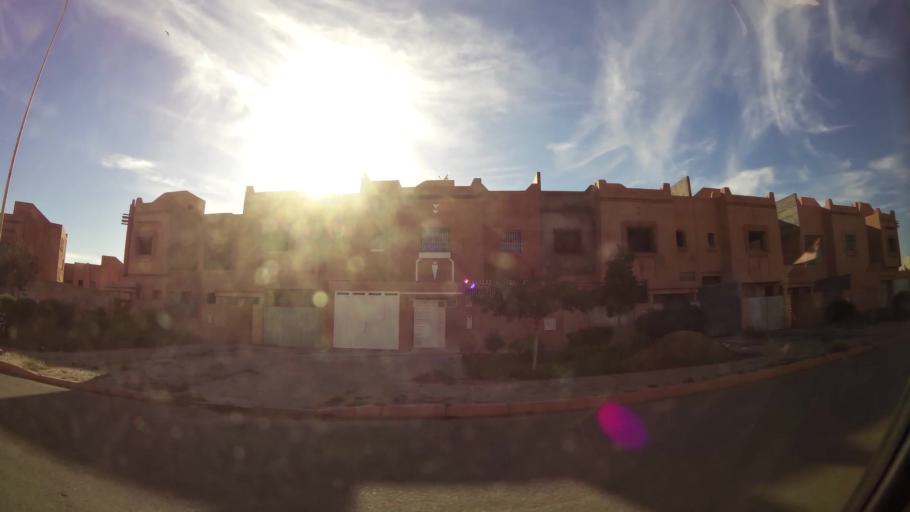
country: MA
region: Marrakech-Tensift-Al Haouz
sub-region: Marrakech
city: Marrakesh
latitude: 31.7505
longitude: -8.1062
